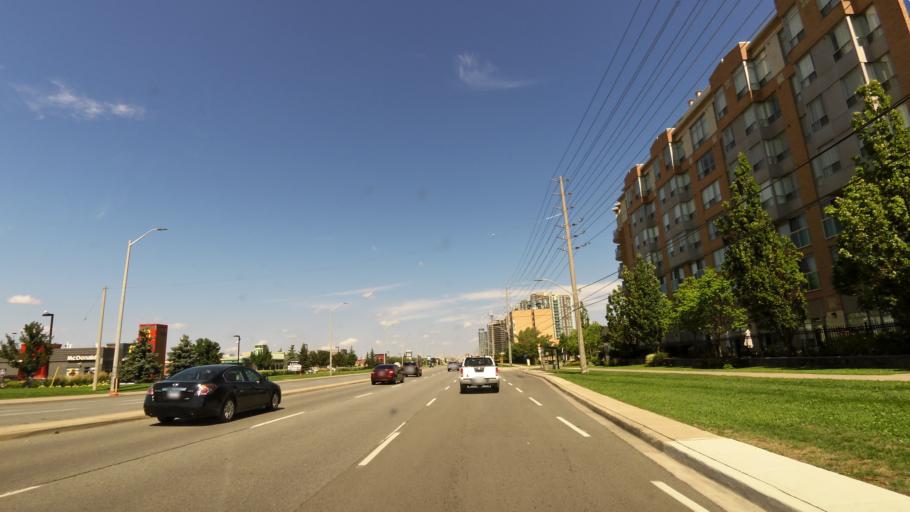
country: CA
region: Ontario
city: Mississauga
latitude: 43.5494
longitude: -79.7172
